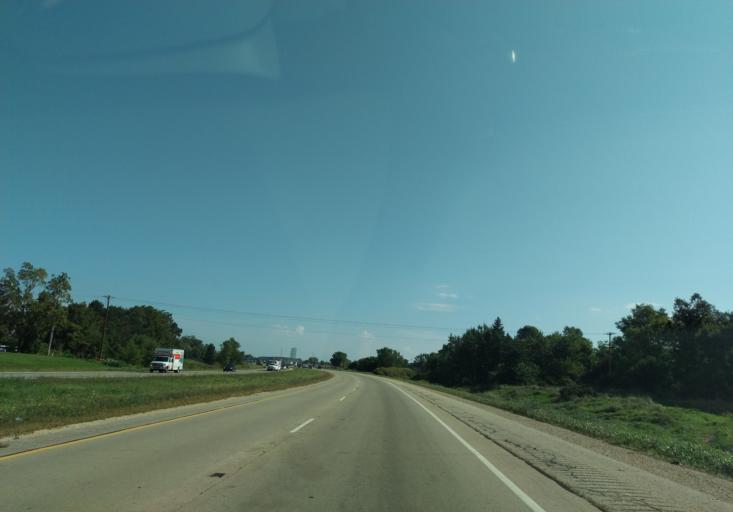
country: US
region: Wisconsin
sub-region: Dane County
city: Fitchburg
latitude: 43.0082
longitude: -89.4786
